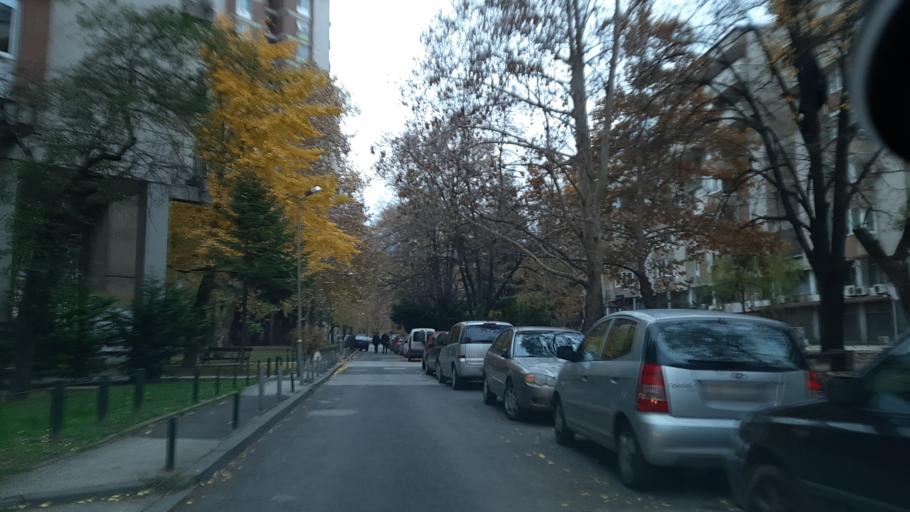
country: MK
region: Karpos
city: Skopje
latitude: 41.9924
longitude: 21.4370
